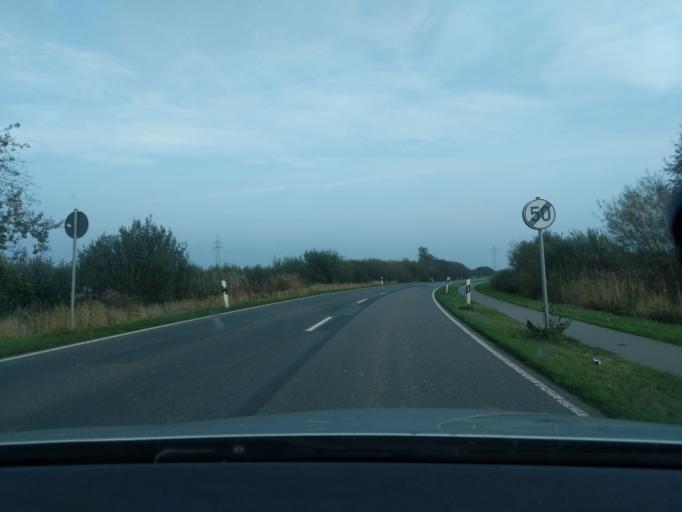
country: DE
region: Lower Saxony
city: Dollern
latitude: 53.5461
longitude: 9.5752
